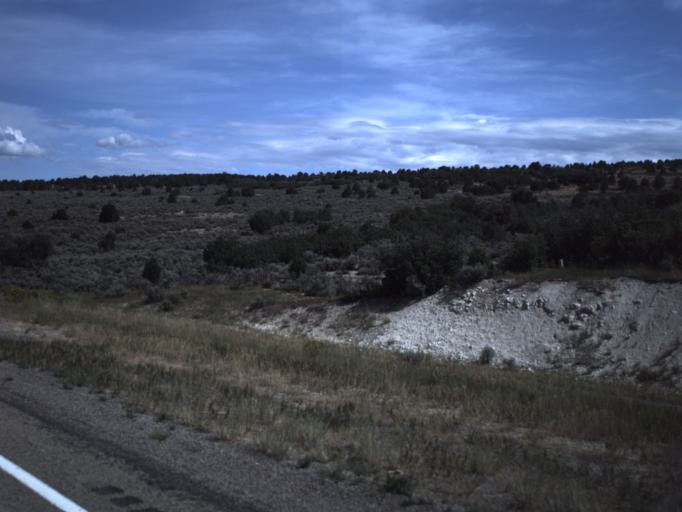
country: US
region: Utah
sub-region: Sanpete County
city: Fairview
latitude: 39.7186
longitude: -111.4709
